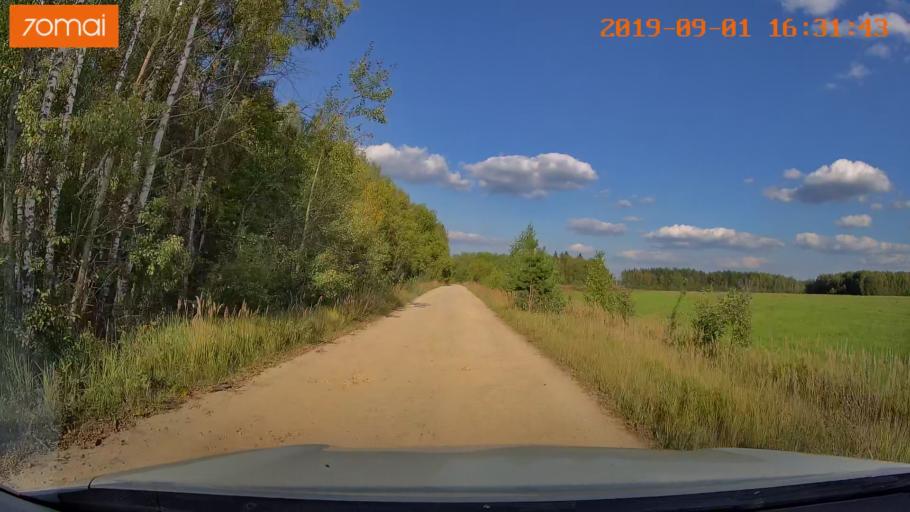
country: RU
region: Kaluga
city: Maloyaroslavets
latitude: 54.9497
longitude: 36.4657
